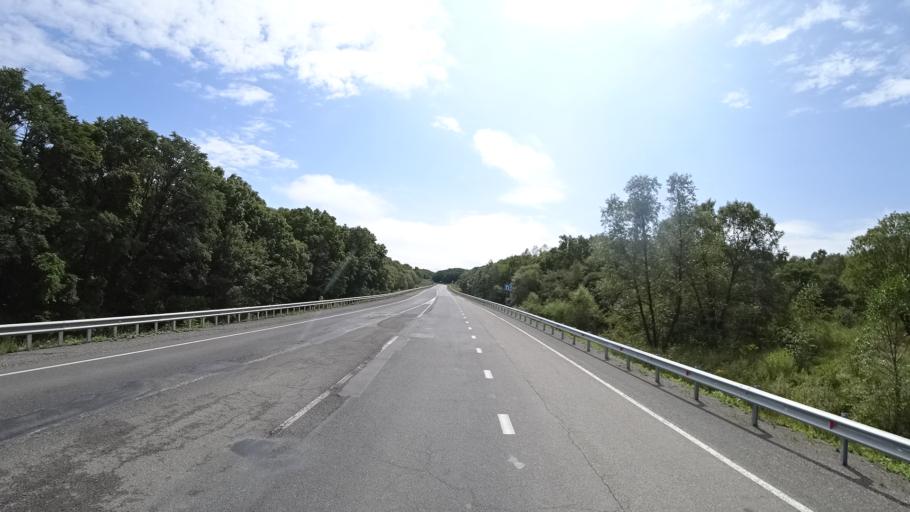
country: RU
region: Primorskiy
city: Lyalichi
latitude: 44.1374
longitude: 132.4284
